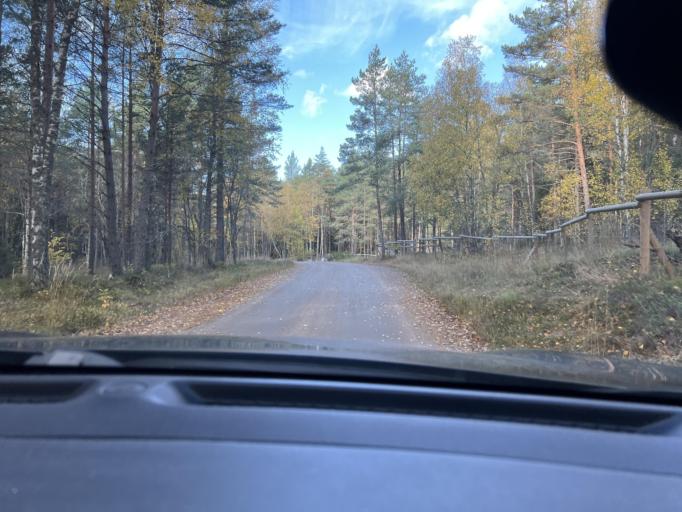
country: SE
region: Stockholm
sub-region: Vallentuna Kommun
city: Vallentuna
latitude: 59.5099
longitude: 18.1253
